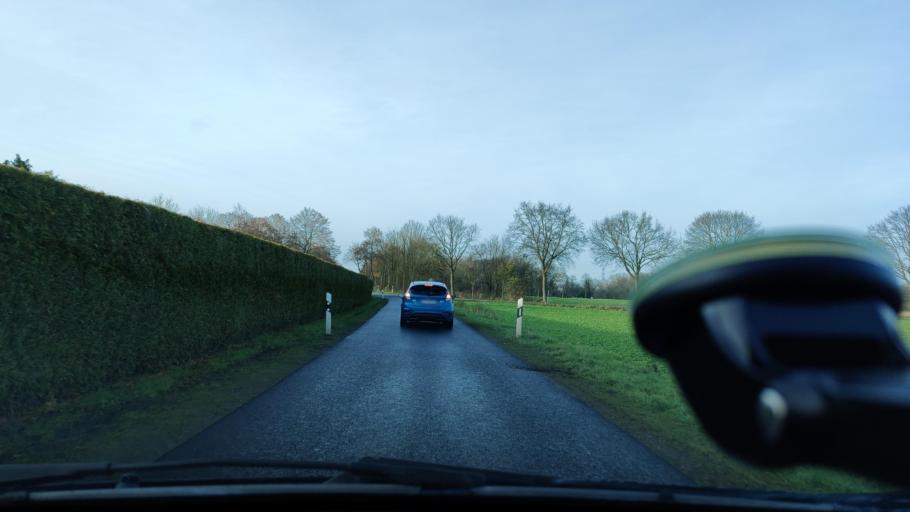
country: DE
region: North Rhine-Westphalia
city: Rees
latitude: 51.7238
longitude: 6.3551
